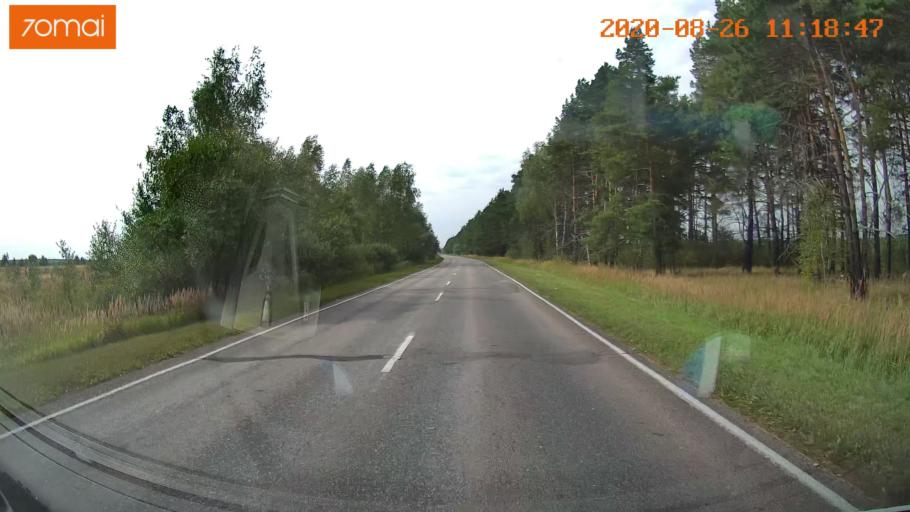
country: RU
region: Rjazan
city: Shilovo
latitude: 54.4067
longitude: 41.0916
